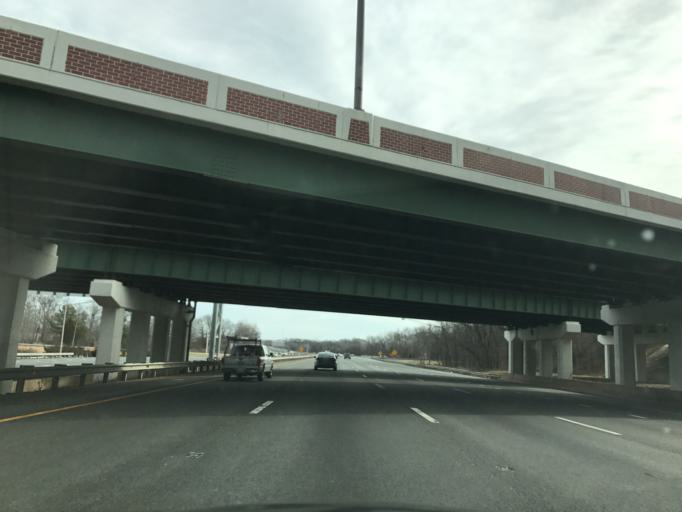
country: US
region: Delaware
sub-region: New Castle County
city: Brookside
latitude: 39.6468
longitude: -75.7465
